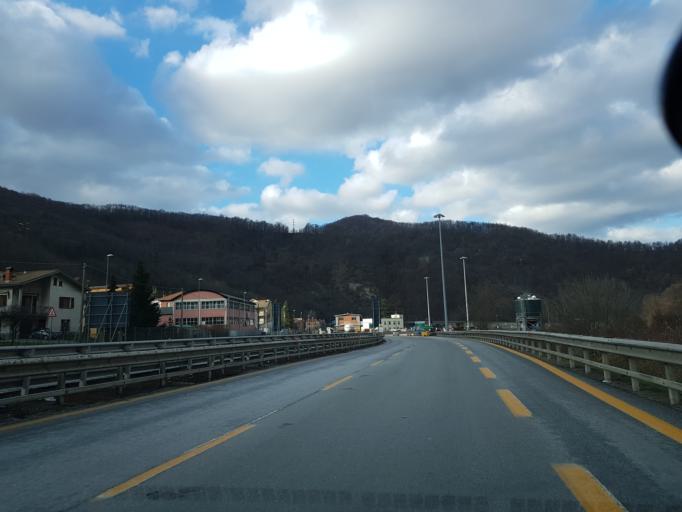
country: IT
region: Liguria
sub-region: Provincia di Genova
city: Ronco Scrivia
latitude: 44.5994
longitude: 8.9530
